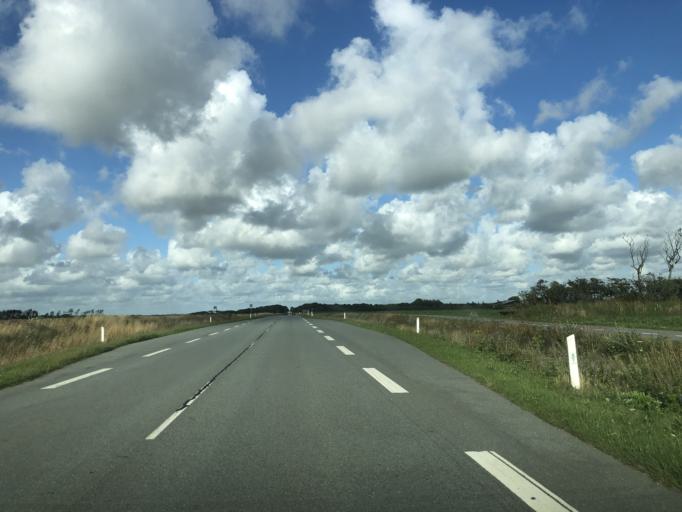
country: DK
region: Central Jutland
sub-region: Lemvig Kommune
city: Lemvig
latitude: 56.4948
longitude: 8.2409
